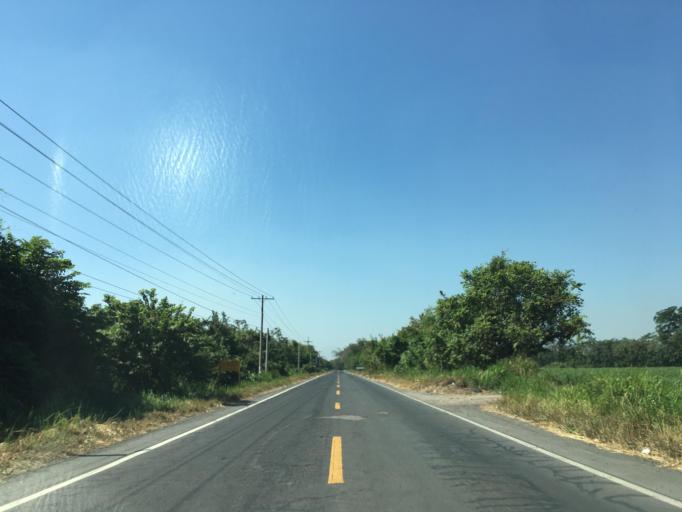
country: GT
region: Escuintla
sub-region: Municipio de Masagua
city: Masagua
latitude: 14.1796
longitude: -90.8674
